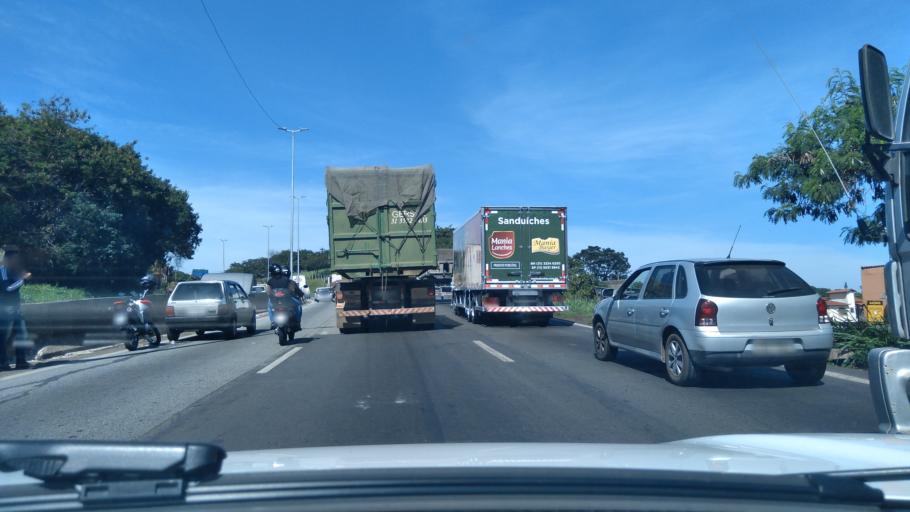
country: BR
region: Minas Gerais
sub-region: Belo Horizonte
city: Belo Horizonte
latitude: -19.8692
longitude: -43.9438
